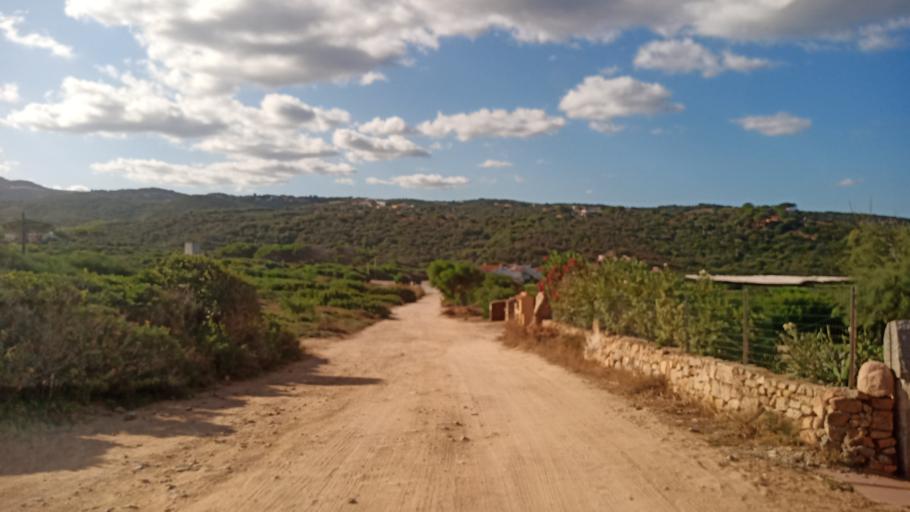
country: IT
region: Sardinia
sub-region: Provincia di Olbia-Tempio
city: Trinita d'Agultu
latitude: 41.0176
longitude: 8.8903
